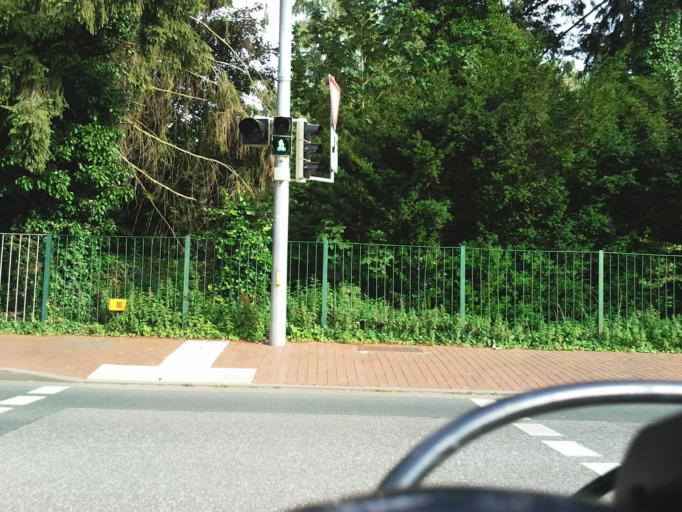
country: DE
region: Mecklenburg-Vorpommern
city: Kritzmow
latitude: 54.0729
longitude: 12.0878
